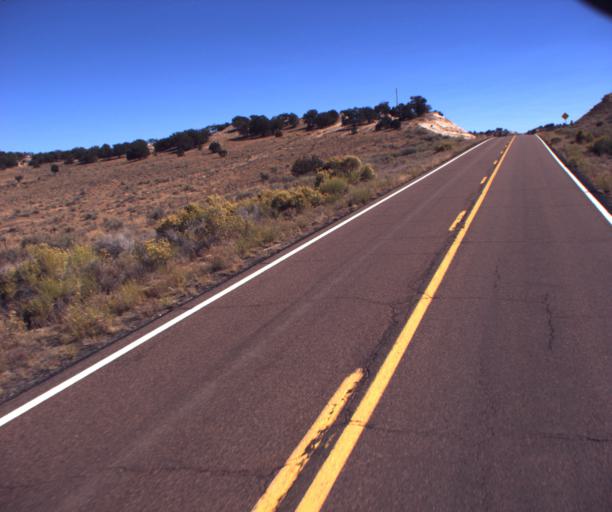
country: US
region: Arizona
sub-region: Navajo County
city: First Mesa
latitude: 35.7639
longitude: -109.9779
